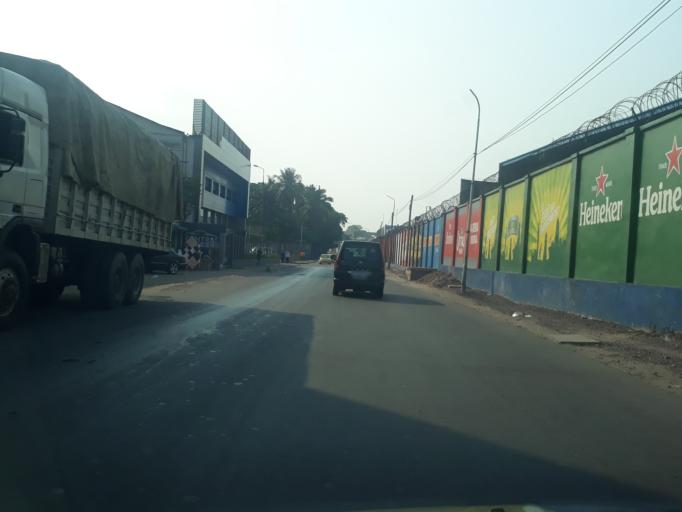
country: CD
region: Kinshasa
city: Kinshasa
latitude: -4.3093
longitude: 15.3276
